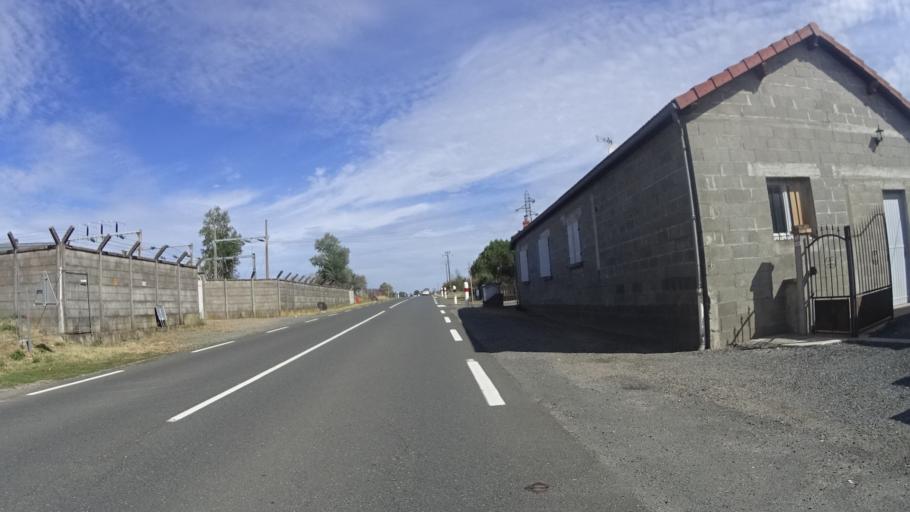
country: FR
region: Bourgogne
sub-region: Departement de Saone-et-Loire
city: Bourbon-Lancy
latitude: 46.6218
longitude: 3.7391
